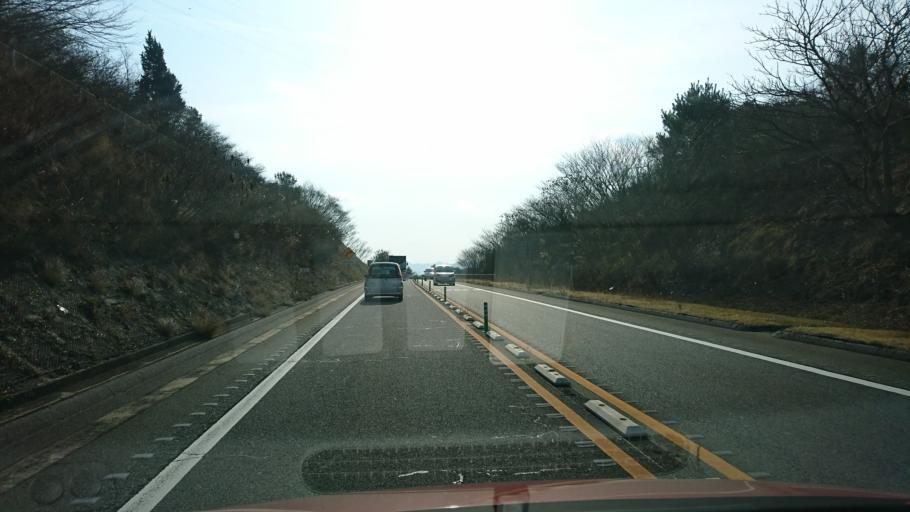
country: JP
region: Hiroshima
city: Onomichi
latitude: 34.3663
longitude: 133.1914
